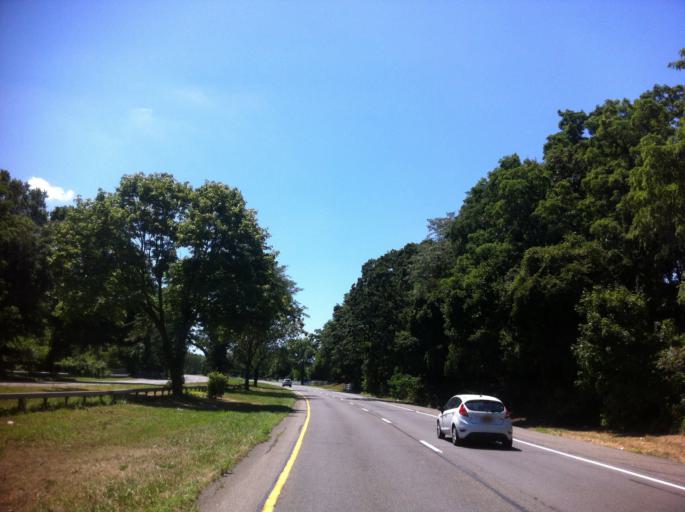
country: US
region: New York
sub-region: Nassau County
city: Glen Head
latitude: 40.8284
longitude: -73.6233
